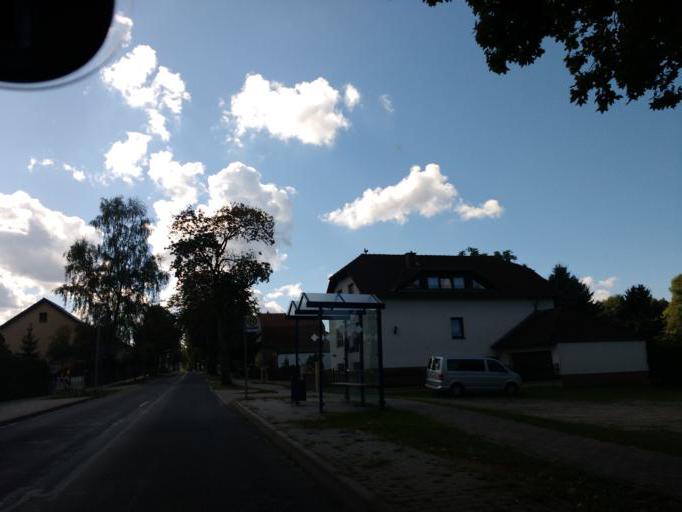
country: DE
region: Brandenburg
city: Mittenwalde
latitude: 52.2100
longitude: 13.5844
